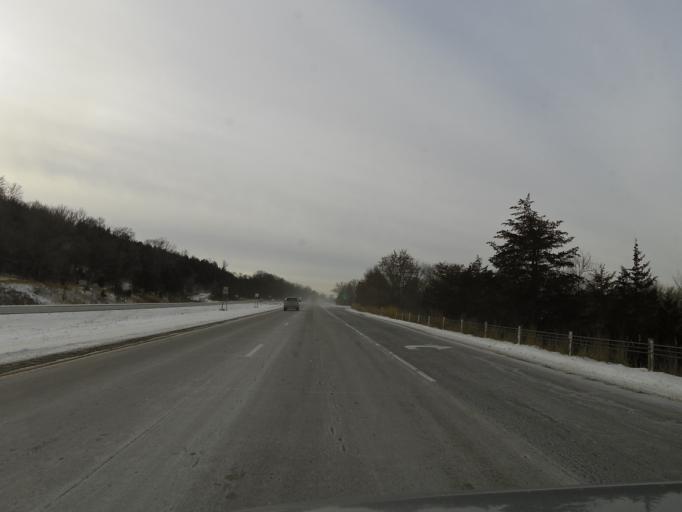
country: US
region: Minnesota
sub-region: Scott County
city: Jordan
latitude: 44.6794
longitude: -93.6211
